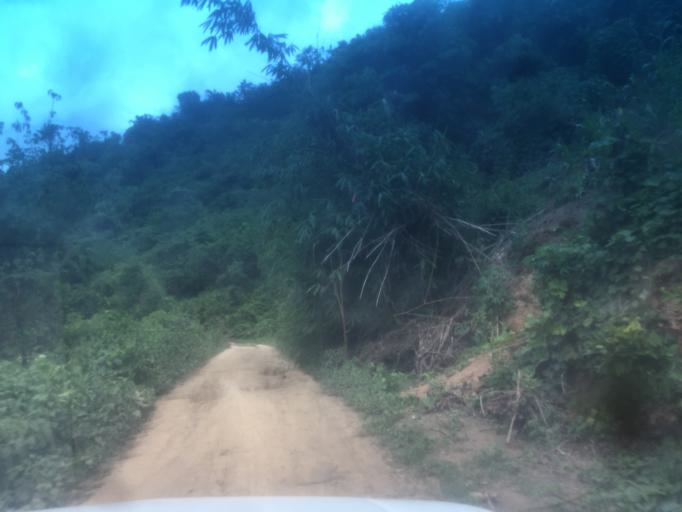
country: LA
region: Phongsali
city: Khoa
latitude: 20.9096
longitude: 102.5531
